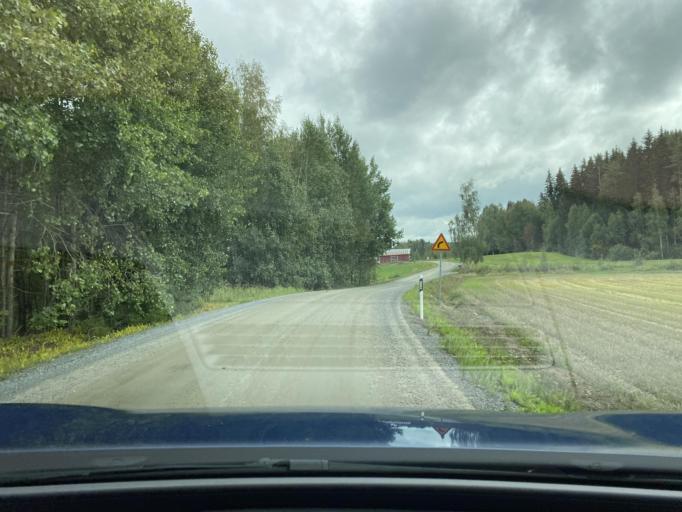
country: FI
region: Pirkanmaa
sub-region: Lounais-Pirkanmaa
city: Vammala
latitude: 61.2627
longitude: 23.0100
